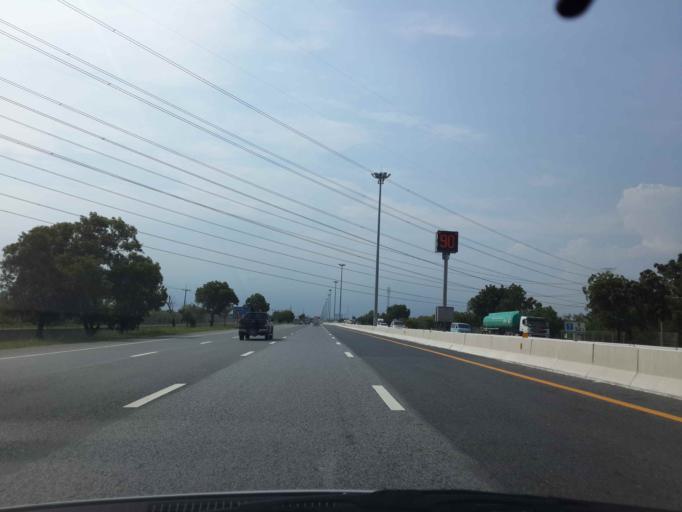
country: TH
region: Chachoengsao
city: Bang Pakong
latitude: 13.5196
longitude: 101.0254
